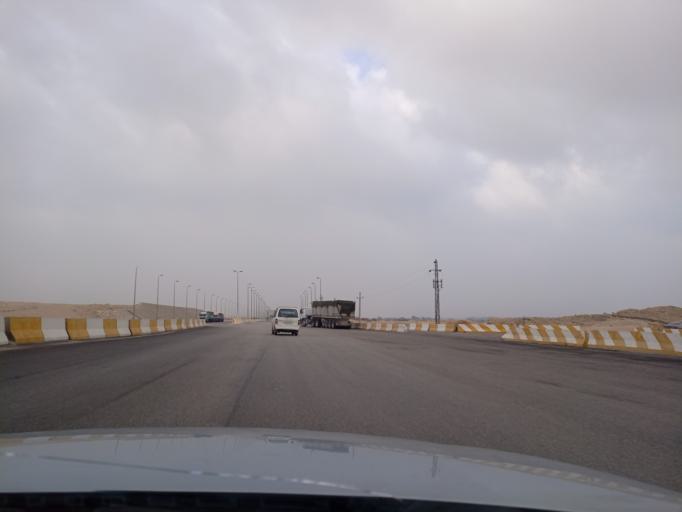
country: EG
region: Muhafazat al Qahirah
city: Halwan
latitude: 29.7143
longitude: 31.3989
